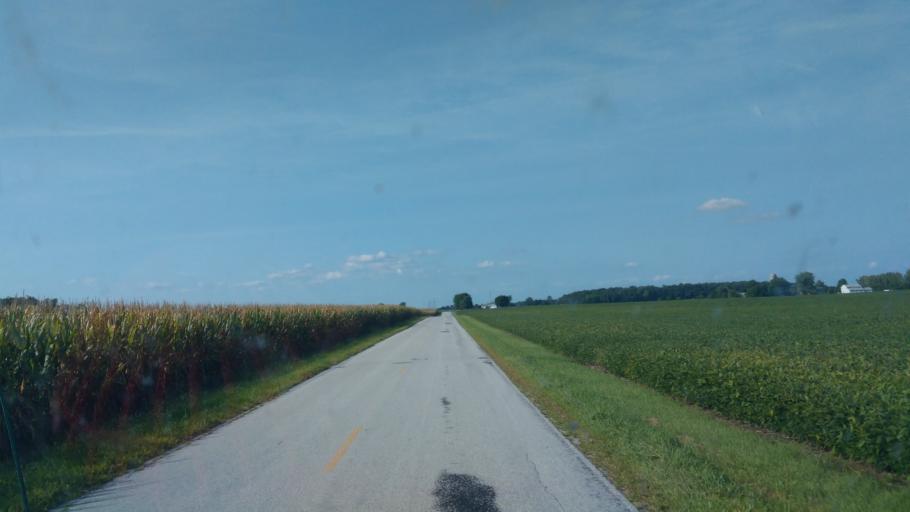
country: US
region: Ohio
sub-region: Hardin County
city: Kenton
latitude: 40.7189
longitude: -83.5725
